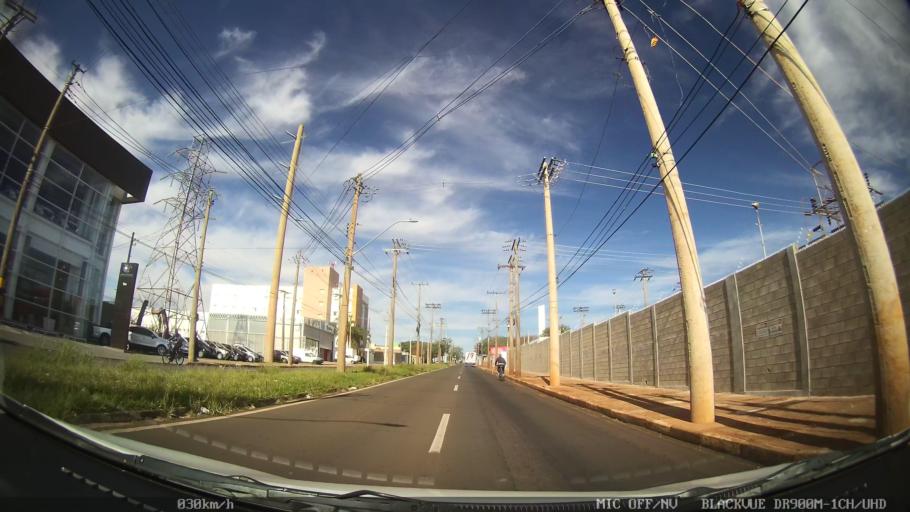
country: BR
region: Sao Paulo
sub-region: Araraquara
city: Araraquara
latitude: -21.8085
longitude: -48.1610
